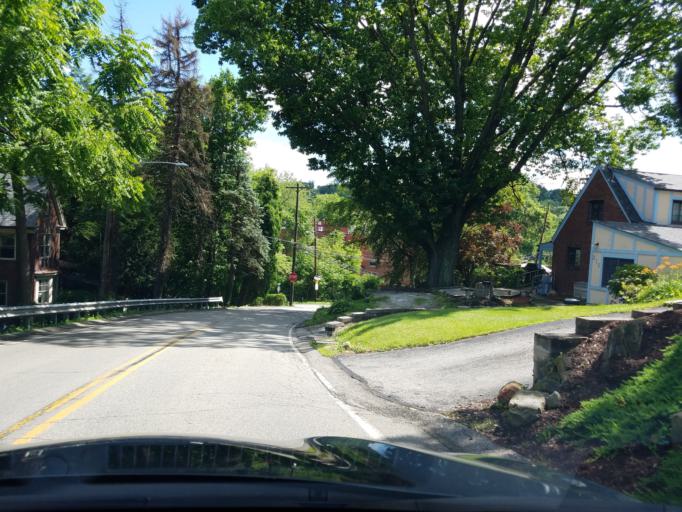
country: US
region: Pennsylvania
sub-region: Allegheny County
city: Braddock Hills
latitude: 40.4239
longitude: -79.8613
